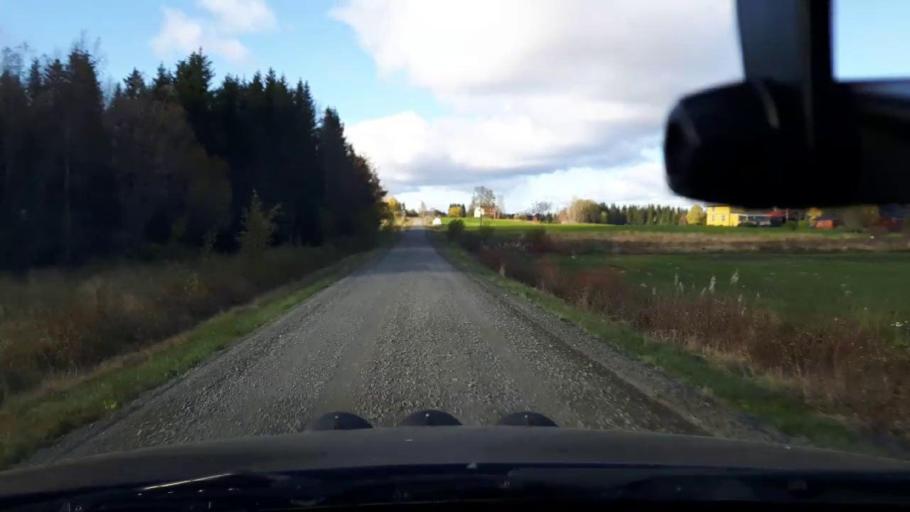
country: SE
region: Jaemtland
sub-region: Bergs Kommun
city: Hoverberg
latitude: 63.0223
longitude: 14.2998
